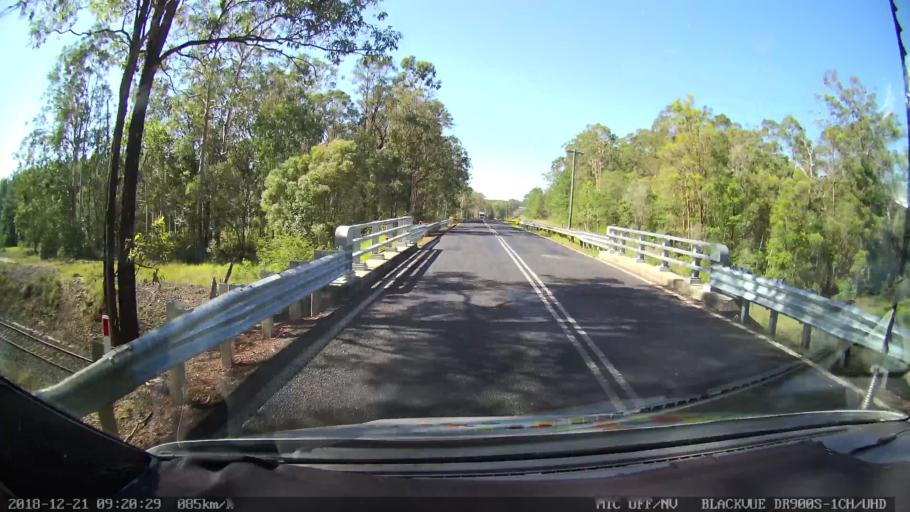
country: AU
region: New South Wales
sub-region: Clarence Valley
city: Maclean
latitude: -29.3153
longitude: 153.0004
